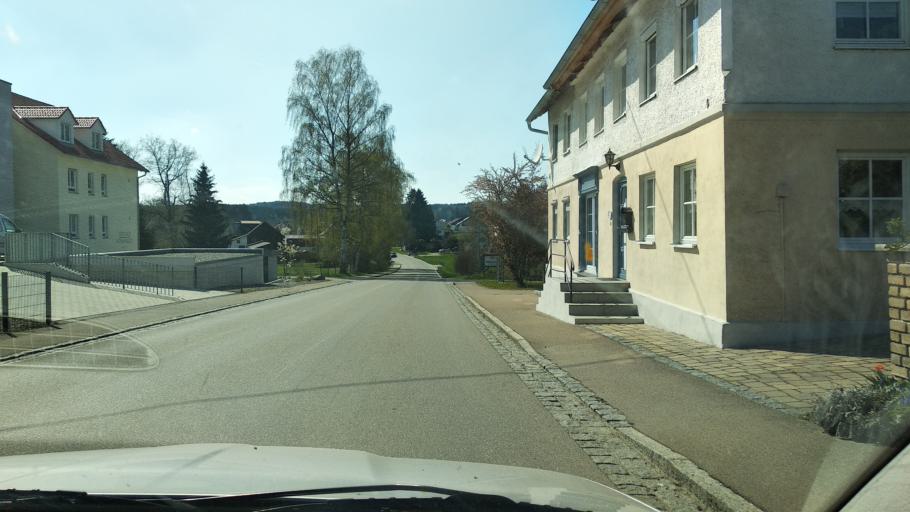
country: DE
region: Bavaria
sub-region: Swabia
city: Stetten
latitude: 48.0451
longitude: 10.4189
